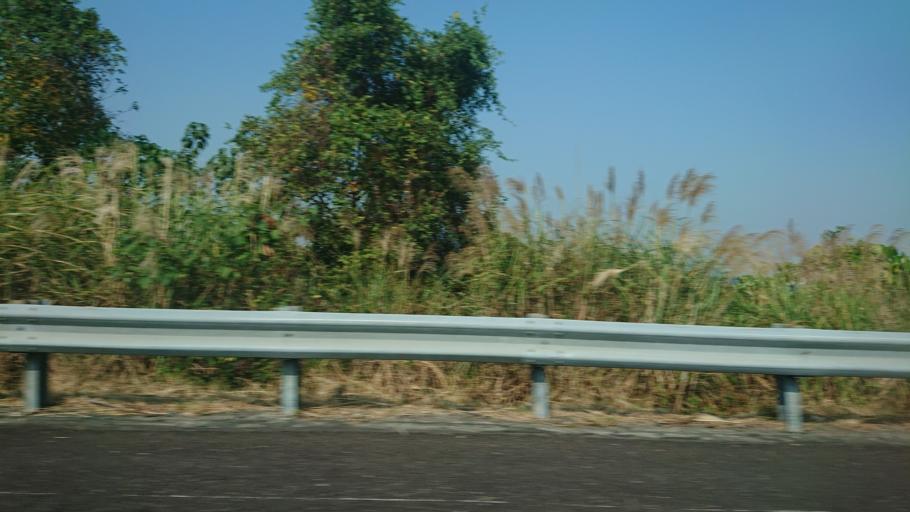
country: TW
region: Taiwan
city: Lugu
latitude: 23.8185
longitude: 120.7037
